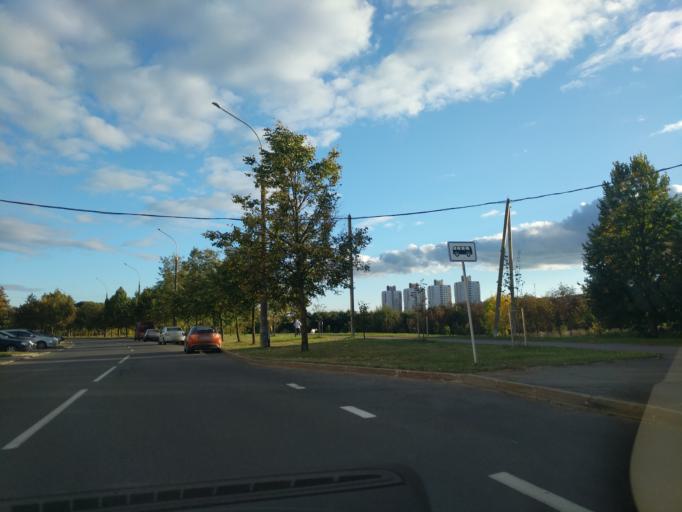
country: BY
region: Minsk
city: Malinovka
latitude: 53.8621
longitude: 27.4486
